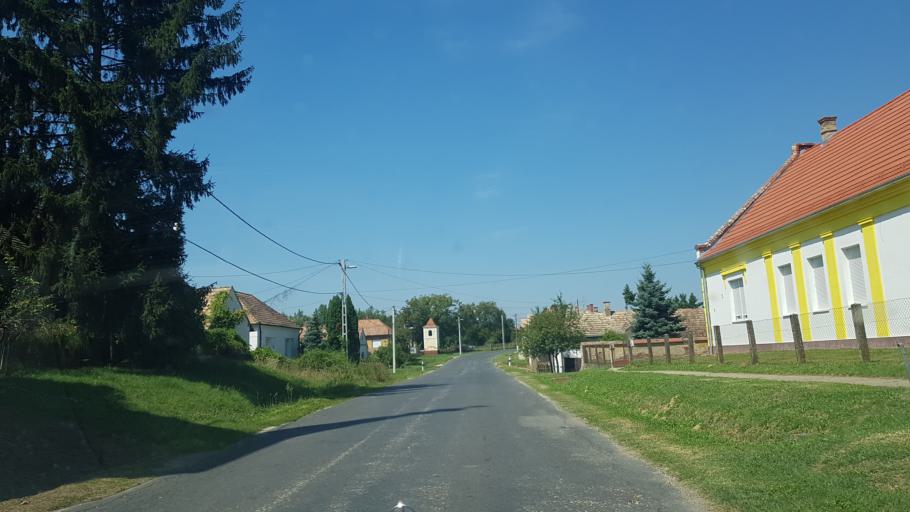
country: HU
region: Somogy
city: Segesd
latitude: 46.3338
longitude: 17.3413
